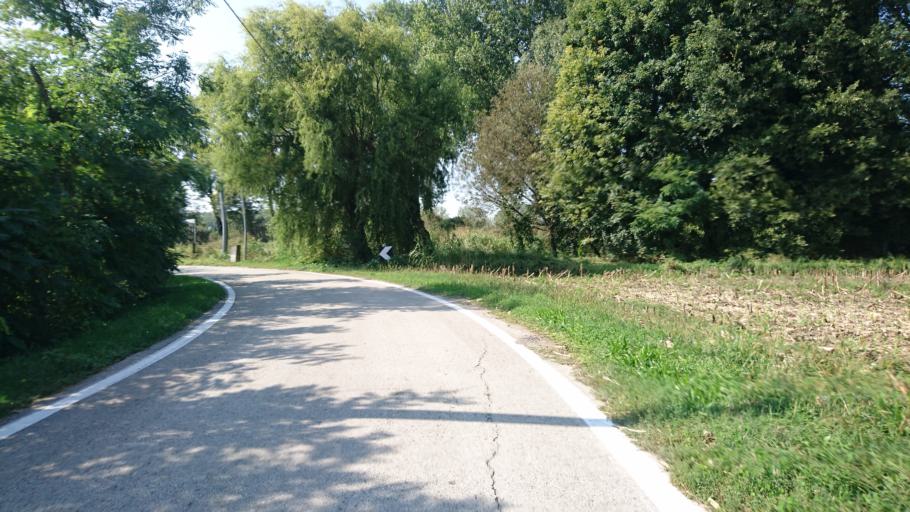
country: IT
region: Veneto
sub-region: Provincia di Padova
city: San Giorgio in Bosco
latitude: 45.5789
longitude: 11.7700
